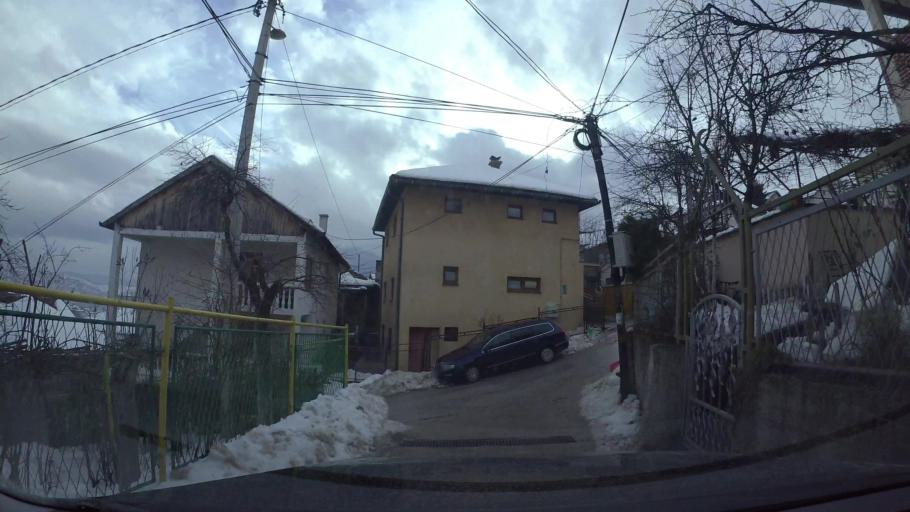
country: BA
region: Federation of Bosnia and Herzegovina
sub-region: Kanton Sarajevo
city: Sarajevo
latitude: 43.8600
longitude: 18.3444
